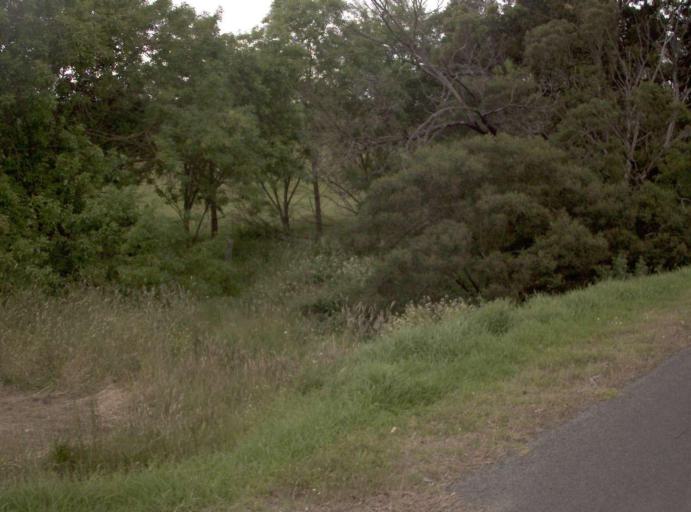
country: AU
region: Victoria
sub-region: Latrobe
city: Traralgon
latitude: -38.5478
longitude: 146.6931
